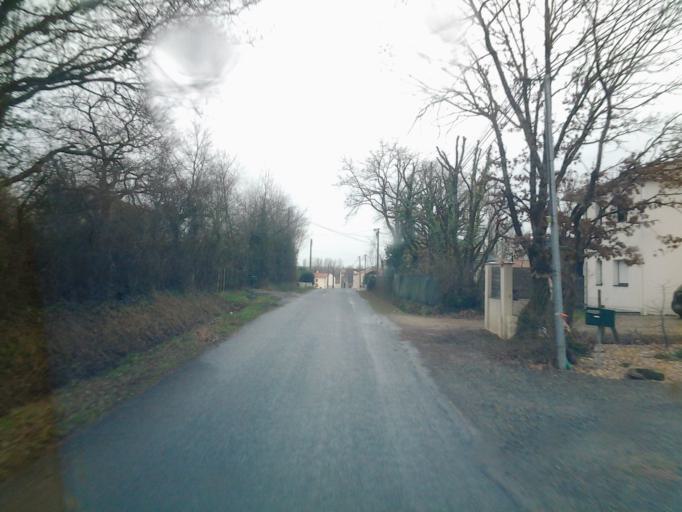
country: FR
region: Pays de la Loire
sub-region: Departement de la Vendee
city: Nesmy
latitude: 46.6432
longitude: -1.3745
